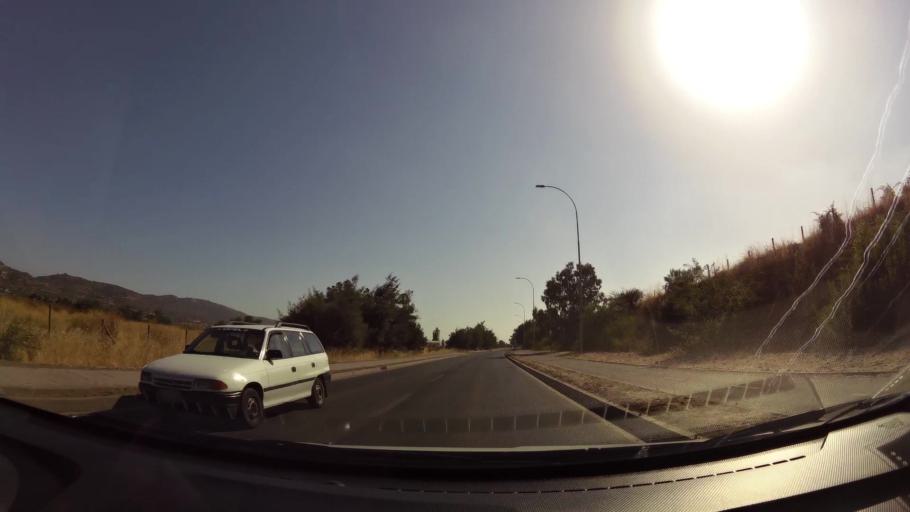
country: CL
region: Maule
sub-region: Provincia de Talca
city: Talca
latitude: -35.4117
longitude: -71.6702
